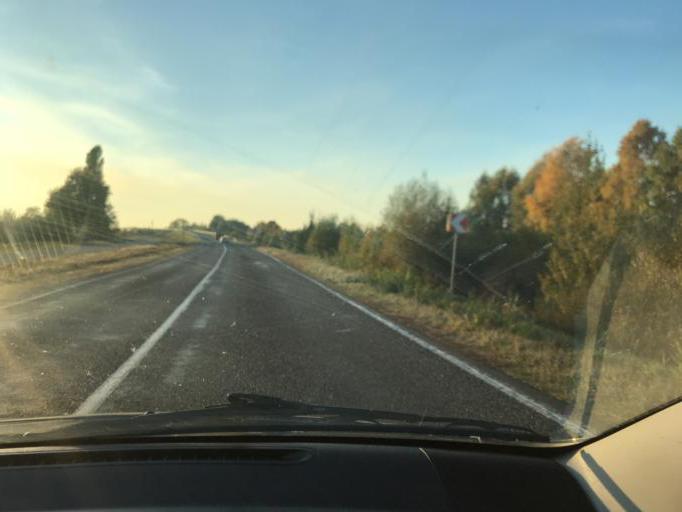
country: BY
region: Brest
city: Pinsk
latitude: 52.0733
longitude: 26.1685
